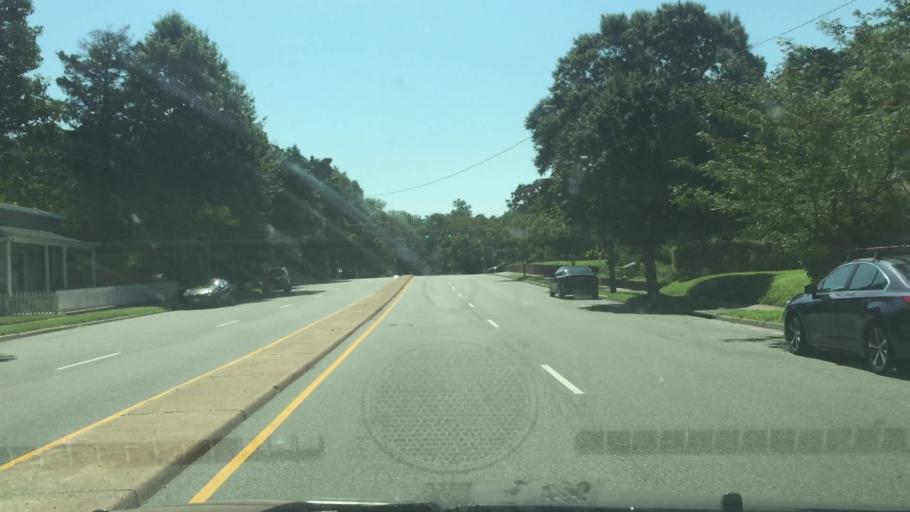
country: US
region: Virginia
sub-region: Henrico County
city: Dumbarton
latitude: 37.5701
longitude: -77.4974
